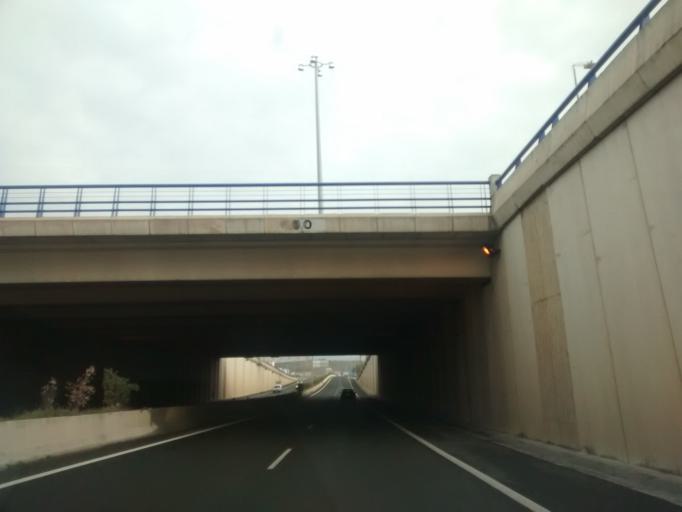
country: ES
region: La Rioja
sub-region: Provincia de La Rioja
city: Logrono
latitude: 42.4612
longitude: -2.4233
